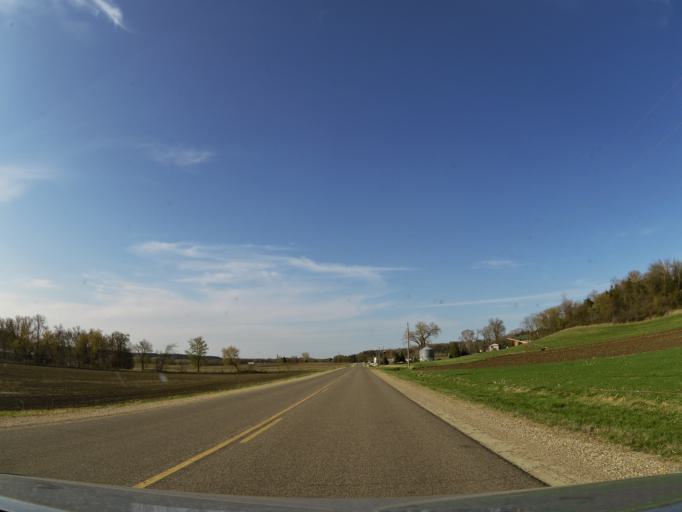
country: US
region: Wisconsin
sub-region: Pierce County
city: River Falls
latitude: 44.7937
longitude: -92.6464
